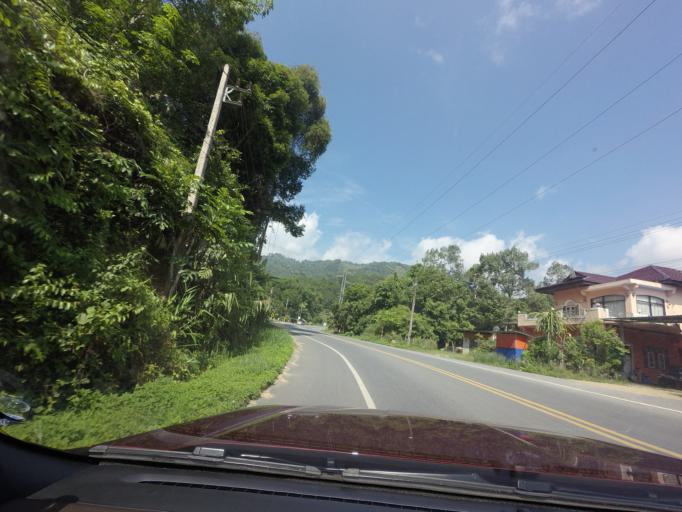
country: TH
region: Yala
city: Betong
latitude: 5.9175
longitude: 101.1729
